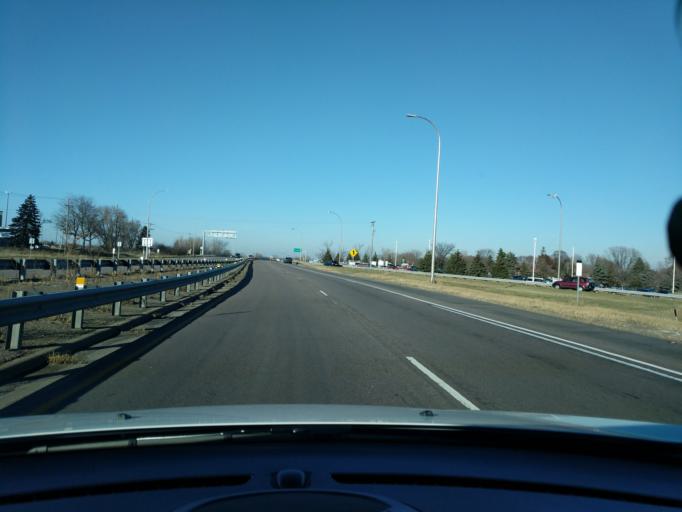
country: US
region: Minnesota
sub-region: Ramsey County
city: Roseville
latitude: 45.0113
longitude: -93.1665
